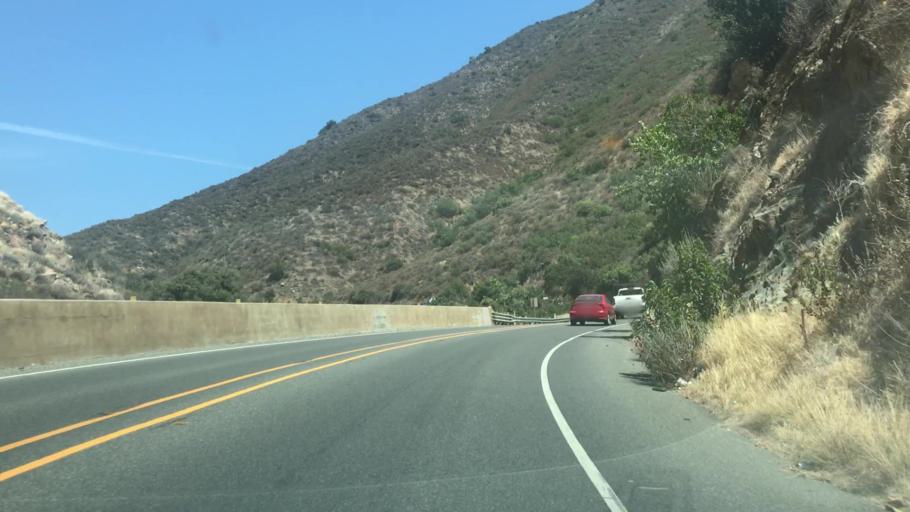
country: US
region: California
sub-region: Orange County
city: Coto De Caza
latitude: 33.5907
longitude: -117.5006
